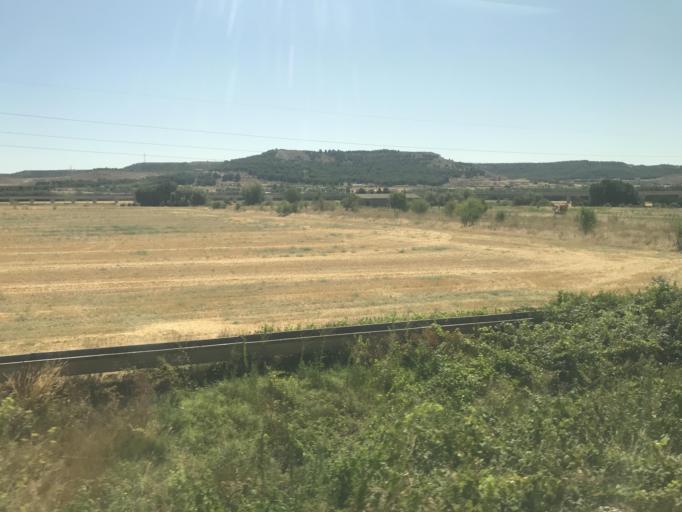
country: ES
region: Castille and Leon
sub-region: Provincia de Valladolid
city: Cabezon
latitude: 41.7204
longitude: -4.6627
